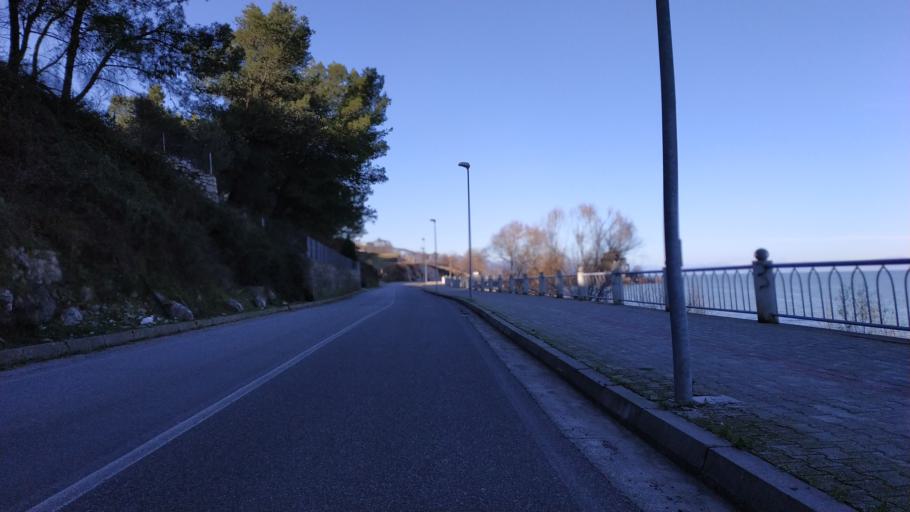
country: AL
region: Shkoder
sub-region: Rrethi i Shkodres
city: Berdica e Madhe
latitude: 42.0576
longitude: 19.4651
